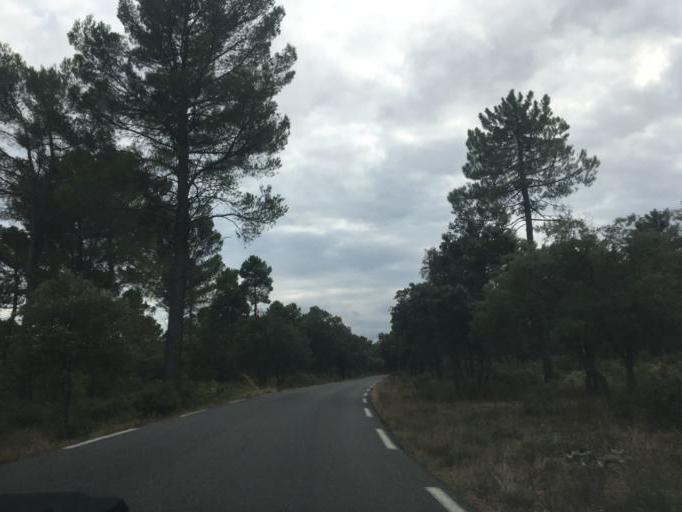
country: FR
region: Provence-Alpes-Cote d'Azur
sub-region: Departement du Var
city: Villecroze
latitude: 43.5551
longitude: 6.3287
